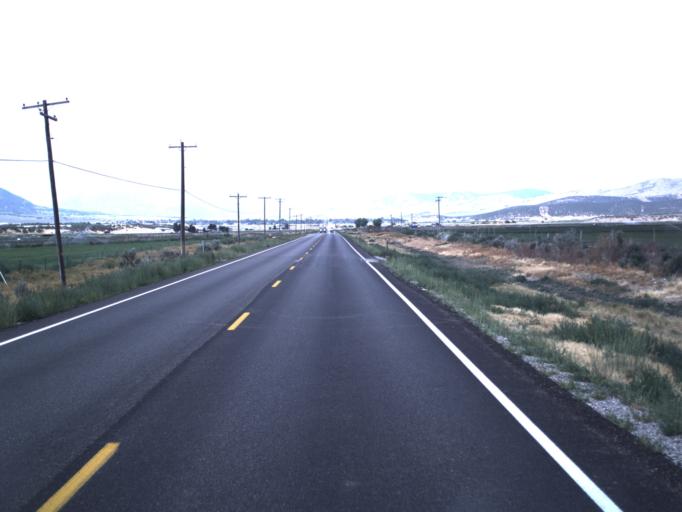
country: US
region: Utah
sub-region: Sanpete County
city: Fountain Green
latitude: 39.5879
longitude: -111.6156
